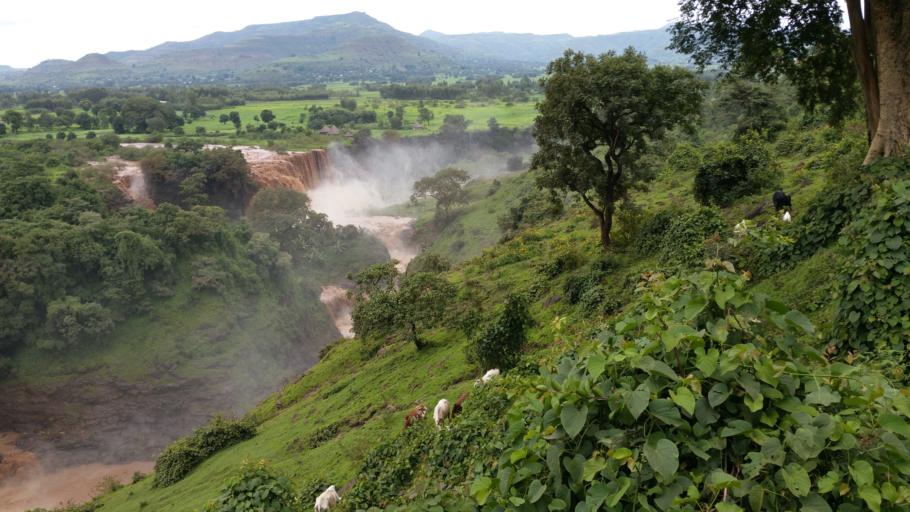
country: ET
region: Amhara
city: Bahir Dar
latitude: 11.4882
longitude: 37.5900
